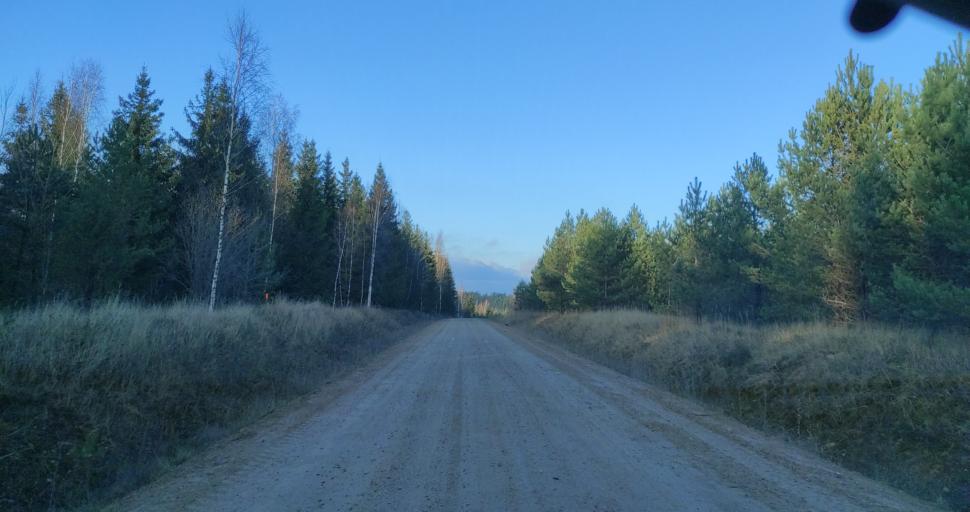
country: LV
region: Kuldigas Rajons
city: Kuldiga
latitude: 57.0558
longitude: 21.8665
